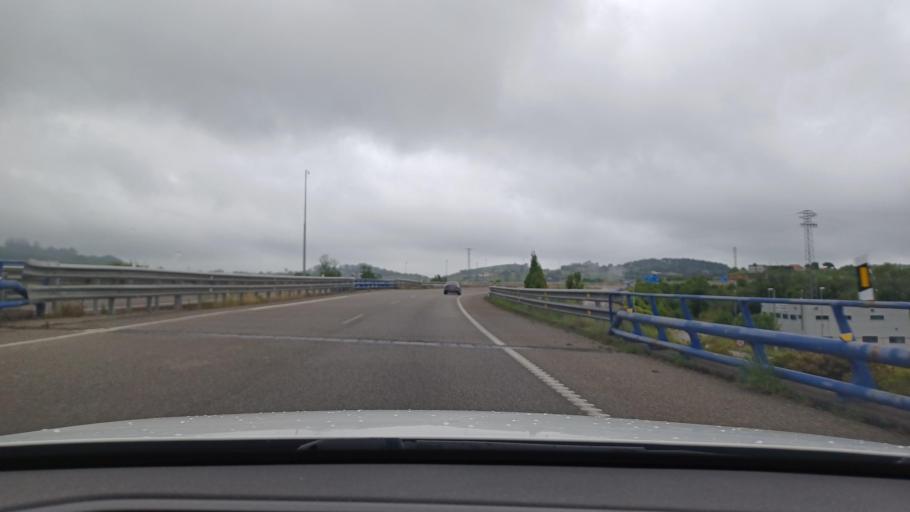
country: ES
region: Asturias
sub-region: Province of Asturias
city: Lugones
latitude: 43.4332
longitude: -5.8168
